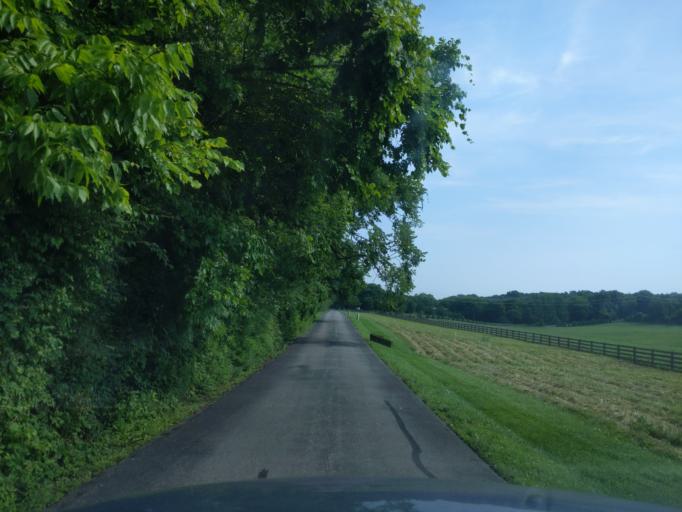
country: US
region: Tennessee
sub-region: Williamson County
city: Brentwood Estates
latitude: 36.0151
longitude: -86.7578
